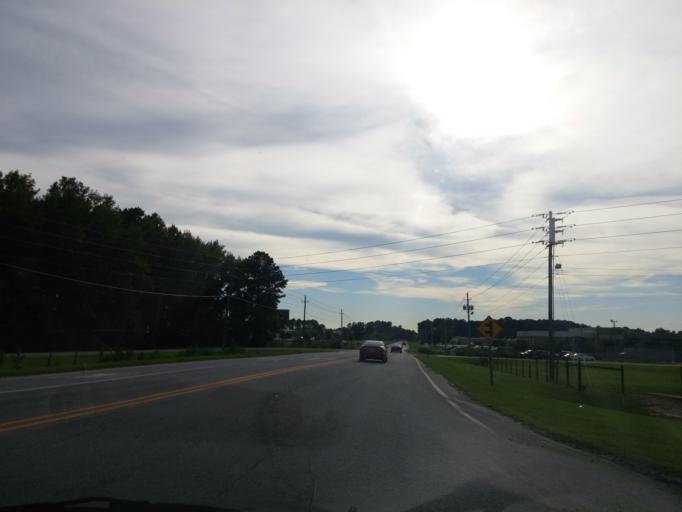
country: US
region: North Carolina
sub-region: Pitt County
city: Greenville
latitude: 35.6532
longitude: -77.3479
